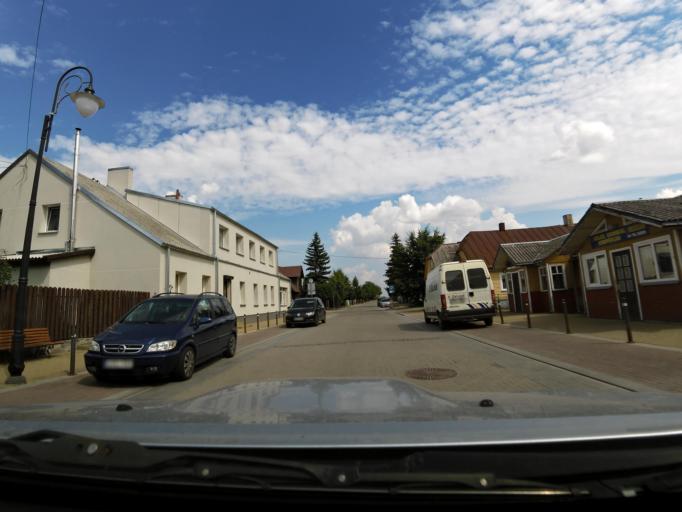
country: LT
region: Taurages apskritis
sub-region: Jurbarkas
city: Jurbarkas
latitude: 55.0765
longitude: 22.7706
